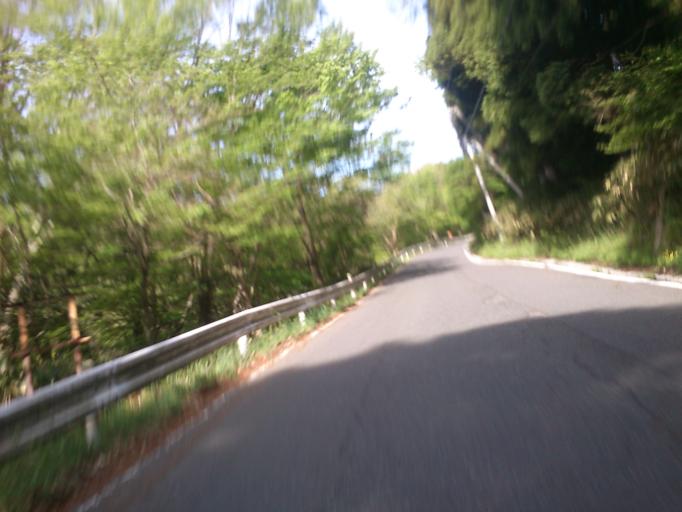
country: JP
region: Kyoto
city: Miyazu
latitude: 35.6395
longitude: 135.1851
